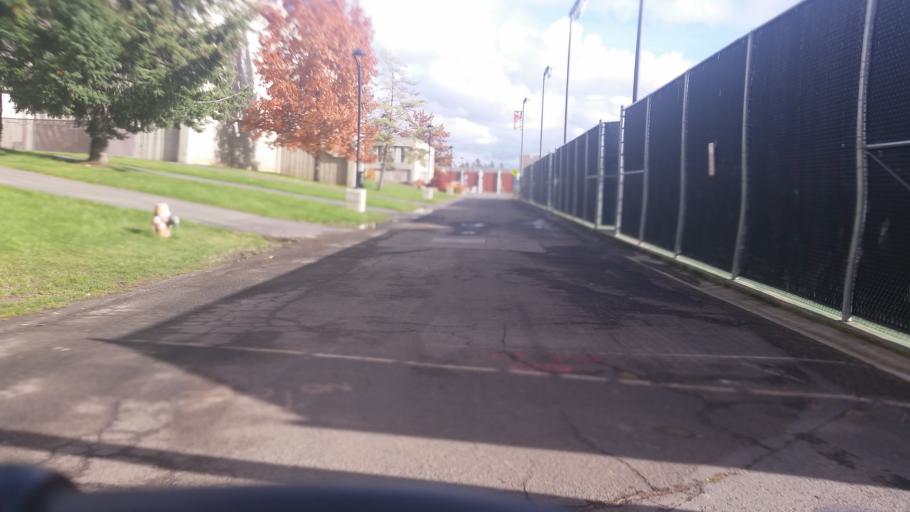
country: US
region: Washington
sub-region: Spokane County
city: Cheney
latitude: 47.4903
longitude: -117.5891
